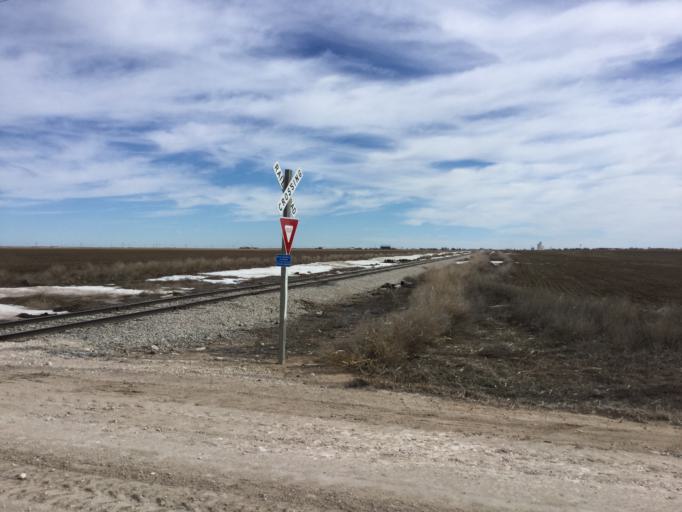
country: US
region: Kansas
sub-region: Lane County
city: Dighton
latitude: 38.4854
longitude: -100.5039
